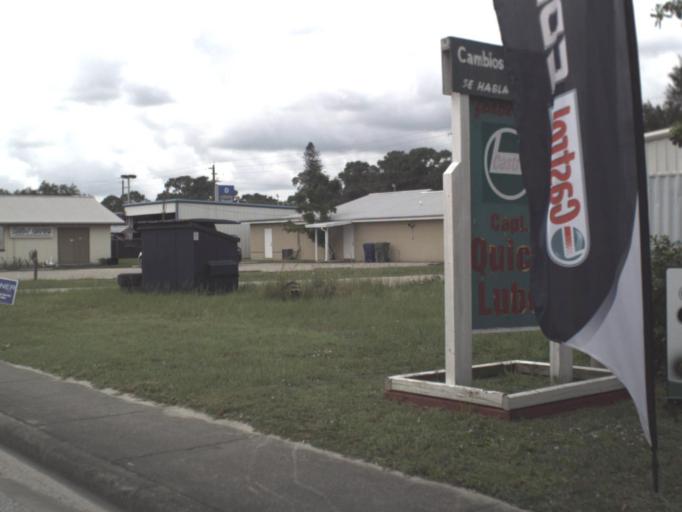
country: US
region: Florida
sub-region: Hendry County
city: LaBelle
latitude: 26.7554
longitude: -81.4374
